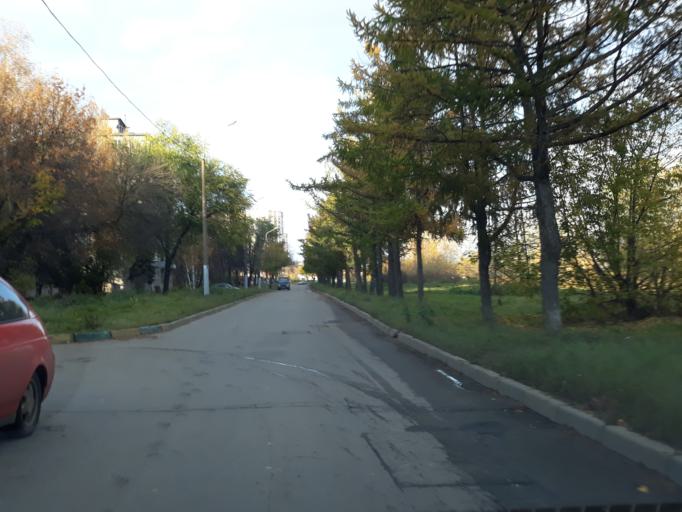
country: RU
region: Nizjnij Novgorod
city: Neklyudovo
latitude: 56.3420
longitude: 43.8715
